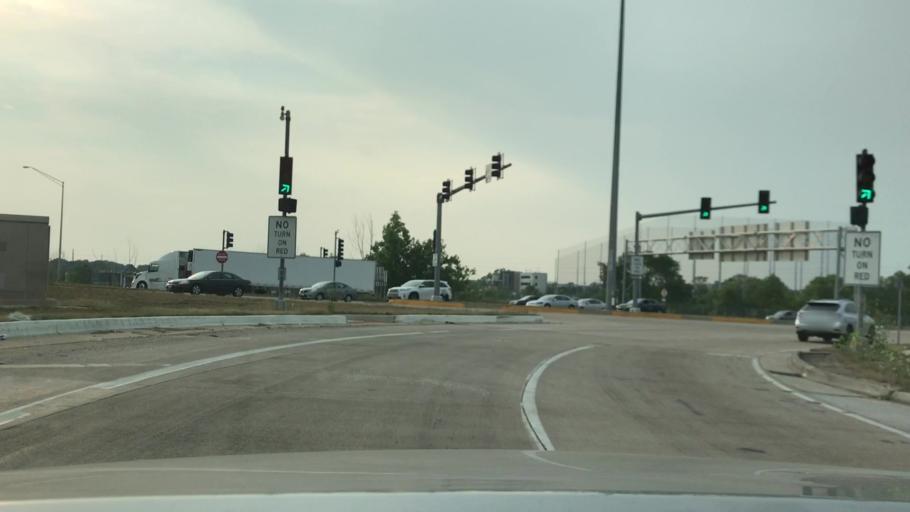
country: US
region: Illinois
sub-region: DuPage County
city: Warrenville
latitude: 41.8050
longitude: -88.2032
